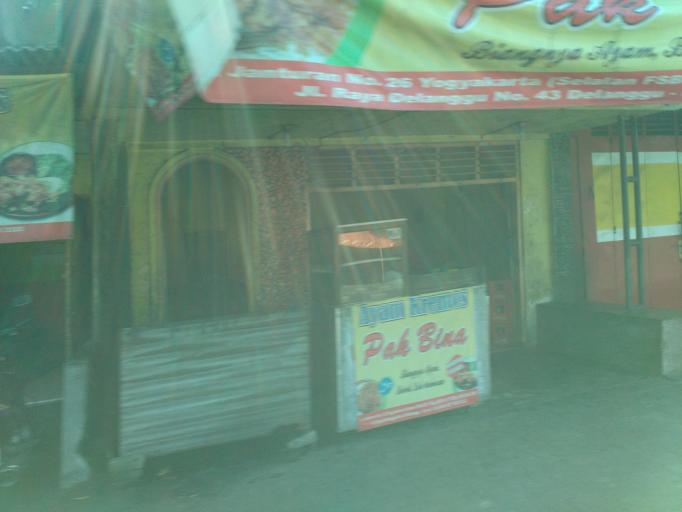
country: ID
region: Central Java
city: Delanggu
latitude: -7.6160
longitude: 110.7005
